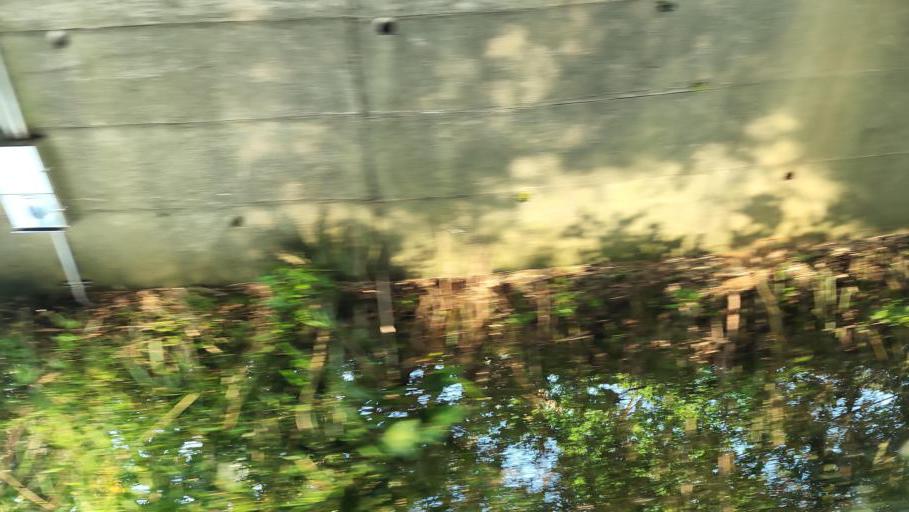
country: TW
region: Taiwan
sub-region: Keelung
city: Keelung
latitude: 25.1828
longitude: 121.6415
